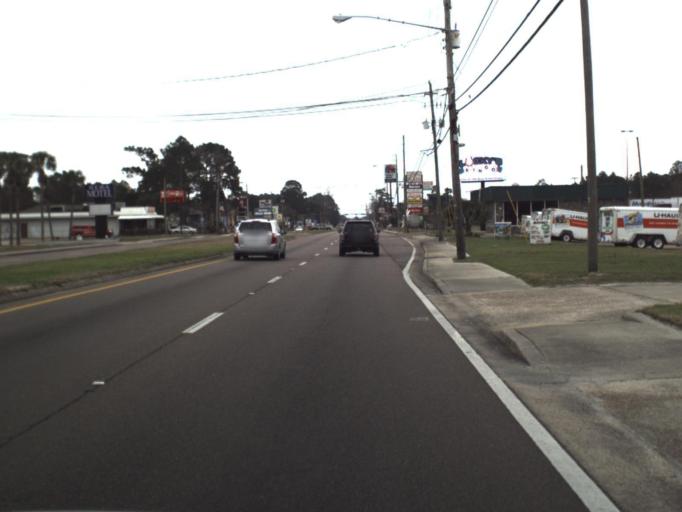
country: US
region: Florida
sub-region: Bay County
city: Parker
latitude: 30.1418
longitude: -85.5913
